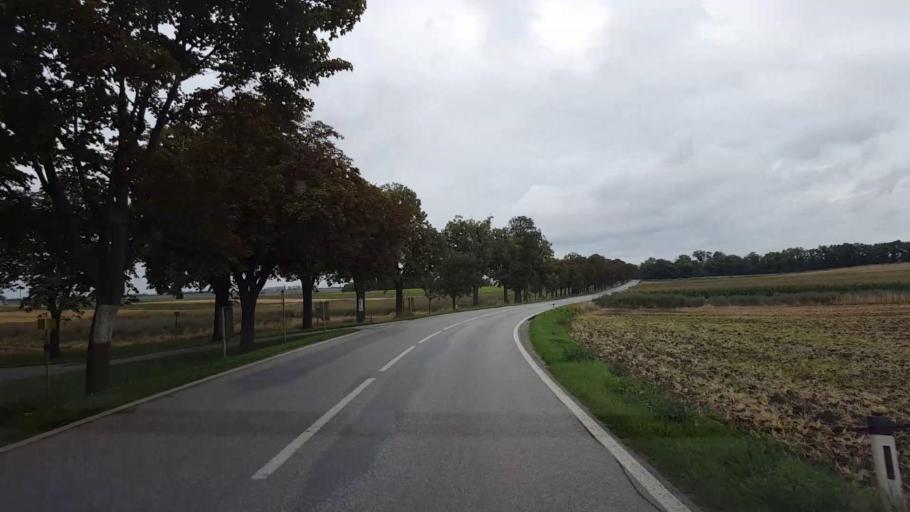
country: AT
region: Lower Austria
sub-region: Politischer Bezirk Wien-Umgebung
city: Rauchenwarth
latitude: 48.0838
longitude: 16.5120
